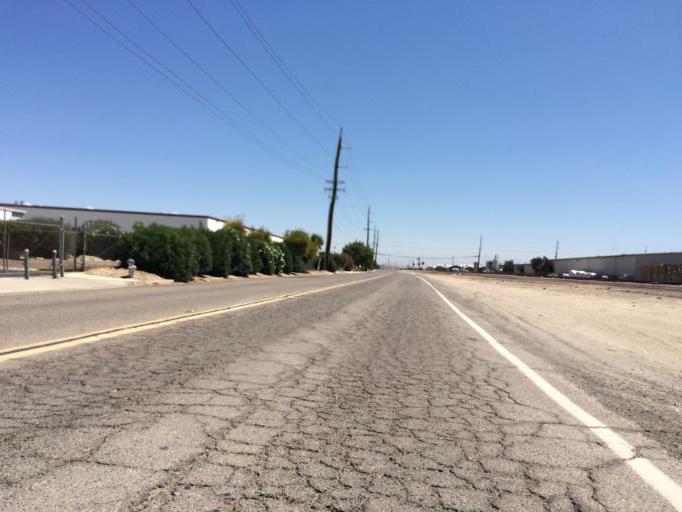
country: US
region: California
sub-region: Fresno County
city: Fresno
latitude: 36.6999
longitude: -119.7493
